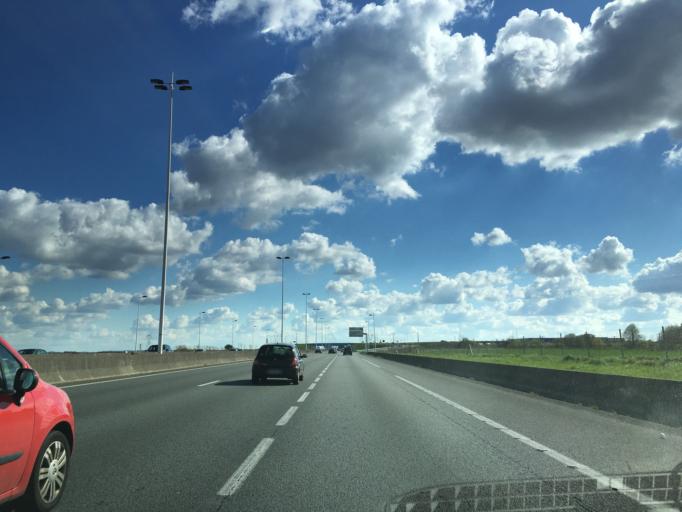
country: FR
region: Nord-Pas-de-Calais
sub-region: Departement du Pas-de-Calais
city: Noyelles-Godault
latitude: 50.4000
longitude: 2.9830
